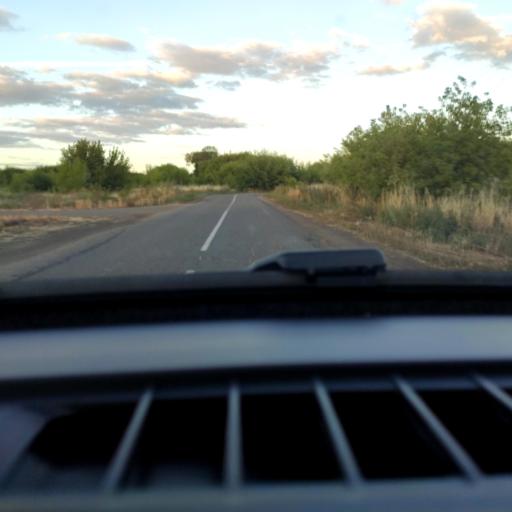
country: RU
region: Voronezj
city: Verkhnyaya Khava
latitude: 51.6132
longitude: 39.8161
